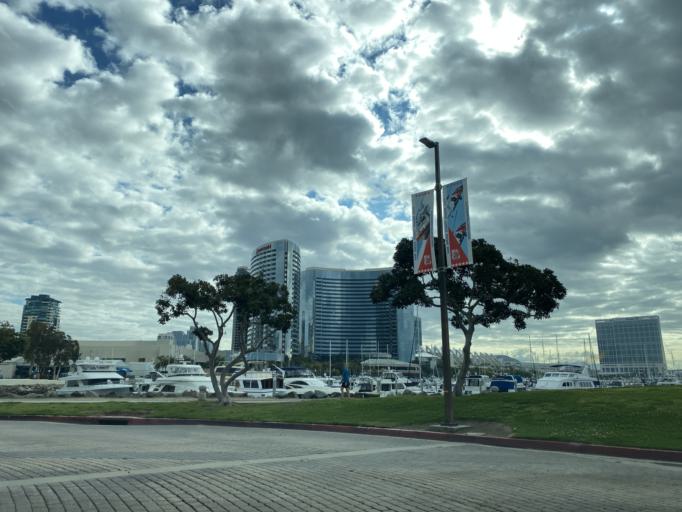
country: US
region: California
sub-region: San Diego County
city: San Diego
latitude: 32.7078
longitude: -117.1695
